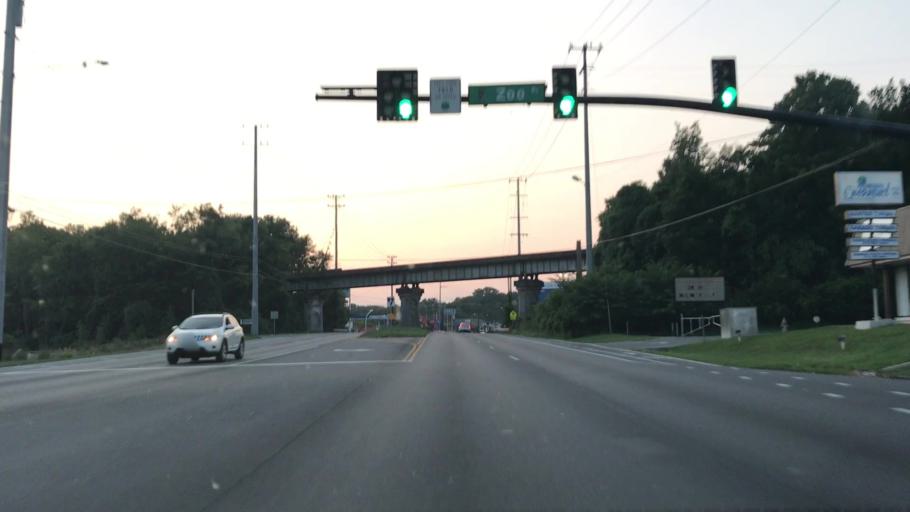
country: US
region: Tennessee
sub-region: Davidson County
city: Oak Hill
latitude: 36.0900
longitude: -86.7336
